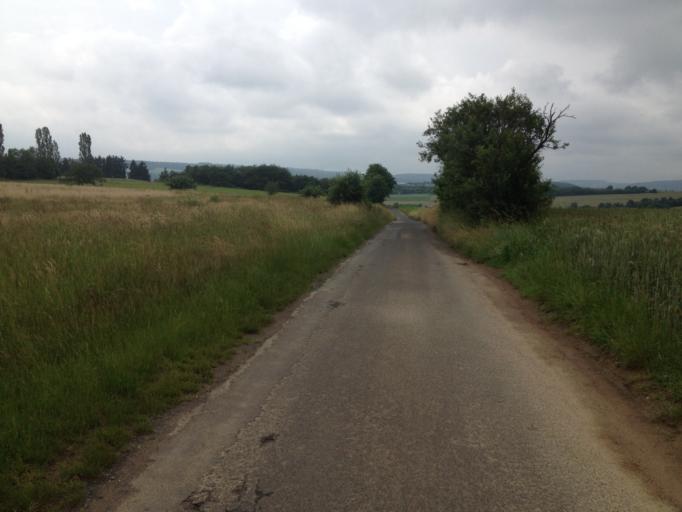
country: DE
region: Saarland
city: Marpingen
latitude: 49.4632
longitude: 7.0458
